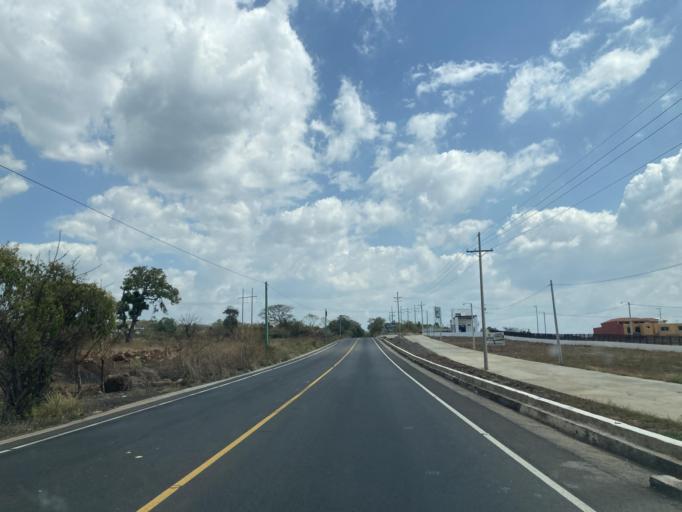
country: GT
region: Santa Rosa
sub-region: Municipio de Taxisco
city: Taxisco
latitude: 14.0643
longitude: -90.4610
